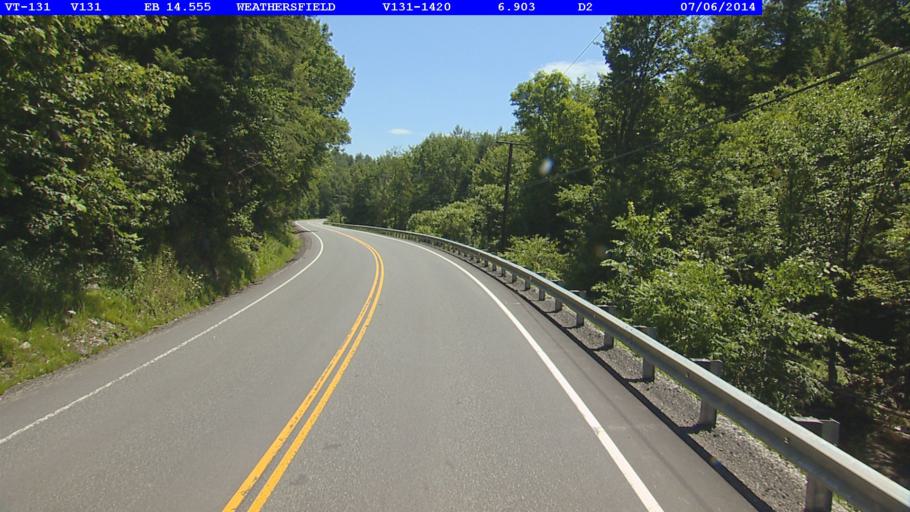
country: US
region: Vermont
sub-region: Windsor County
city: Windsor
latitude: 43.4067
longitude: -72.4376
